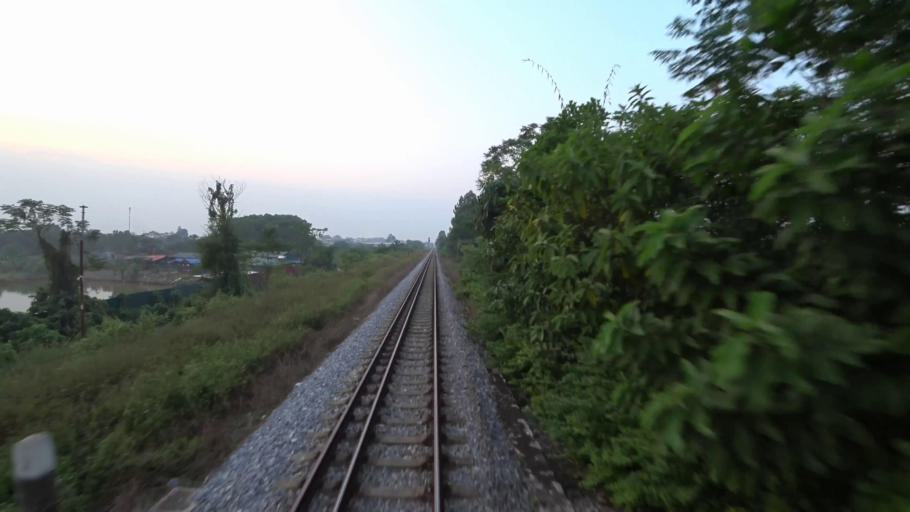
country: VN
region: Ha Noi
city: Dong Anh
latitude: 21.1366
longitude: 105.8698
